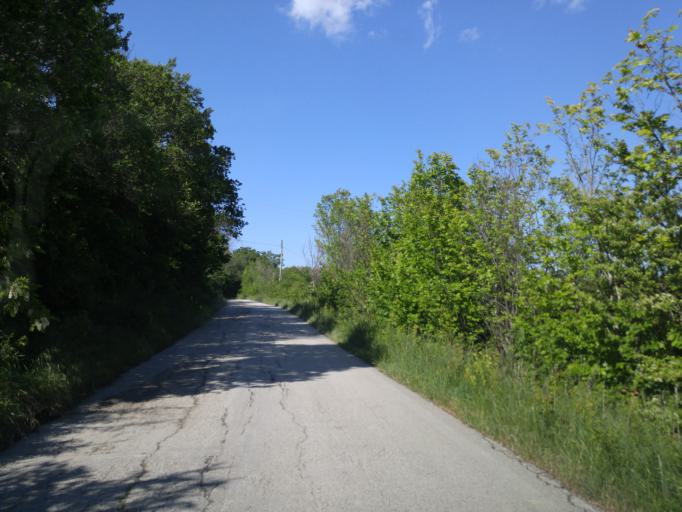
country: IT
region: The Marches
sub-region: Provincia di Pesaro e Urbino
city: Lucrezia
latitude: 43.7915
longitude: 12.9124
